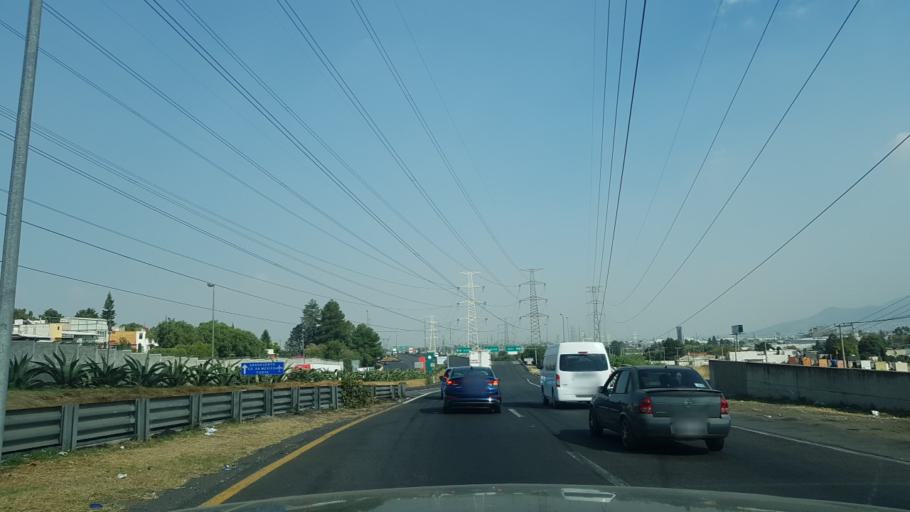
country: MX
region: Mexico
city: Cuautitlan Izcalli
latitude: 19.6353
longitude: -99.1993
